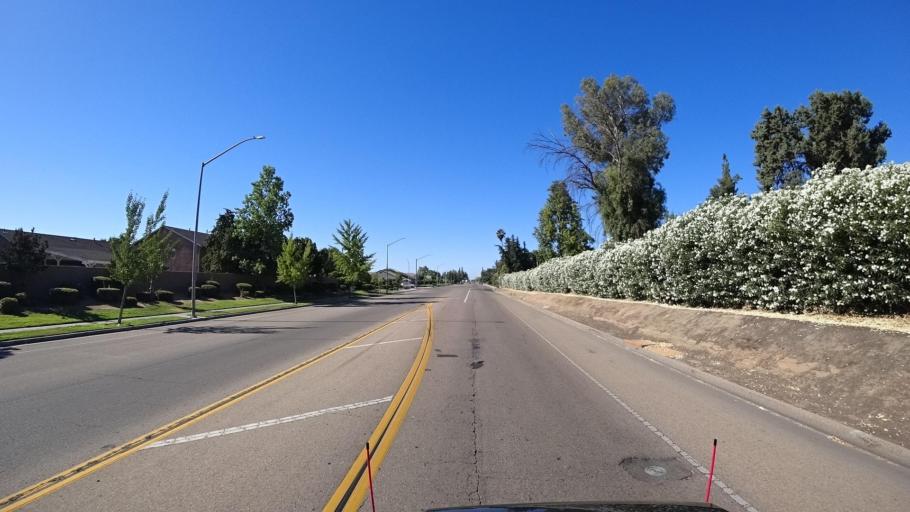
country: US
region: California
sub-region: Fresno County
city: Sunnyside
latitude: 36.7271
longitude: -119.6822
